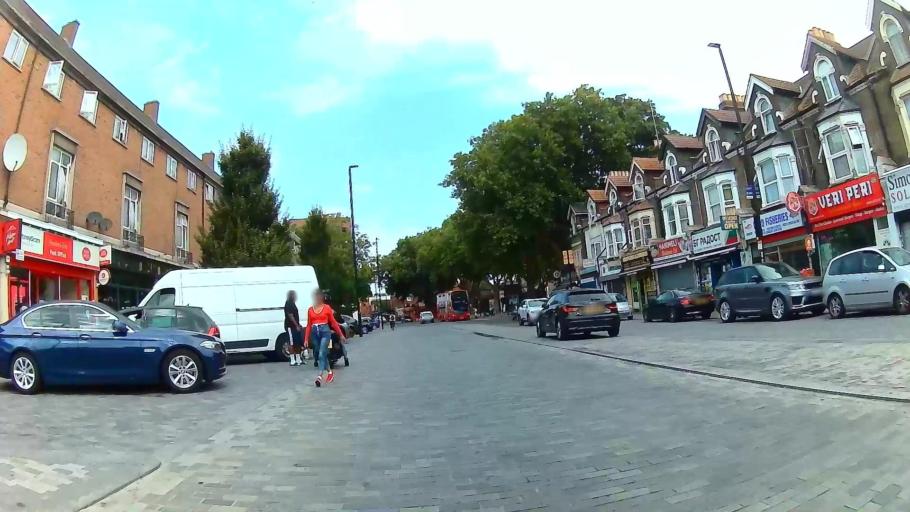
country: GB
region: England
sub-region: Greater London
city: Enfield
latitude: 51.6442
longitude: -0.0465
